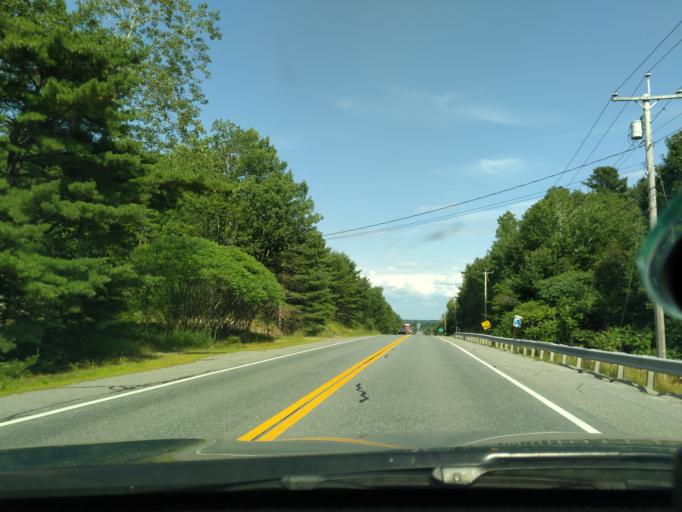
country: US
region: Maine
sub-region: Hancock County
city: Surry
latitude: 44.5398
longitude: -68.4953
